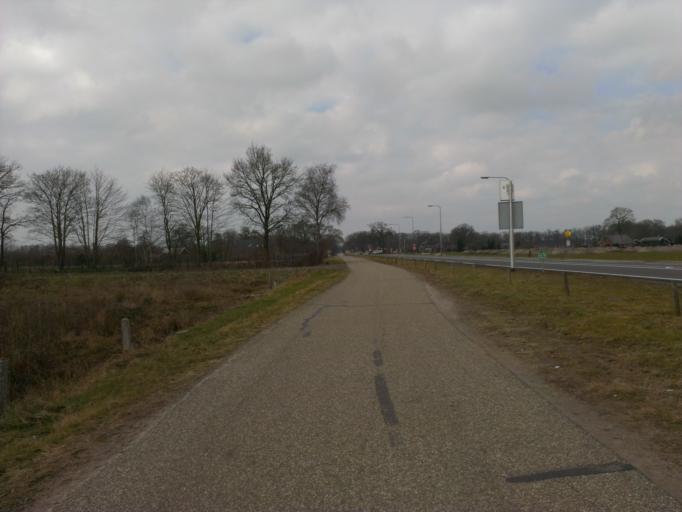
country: NL
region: Overijssel
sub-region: Gemeente Almelo
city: Almelo
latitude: 52.3324
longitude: 6.7067
